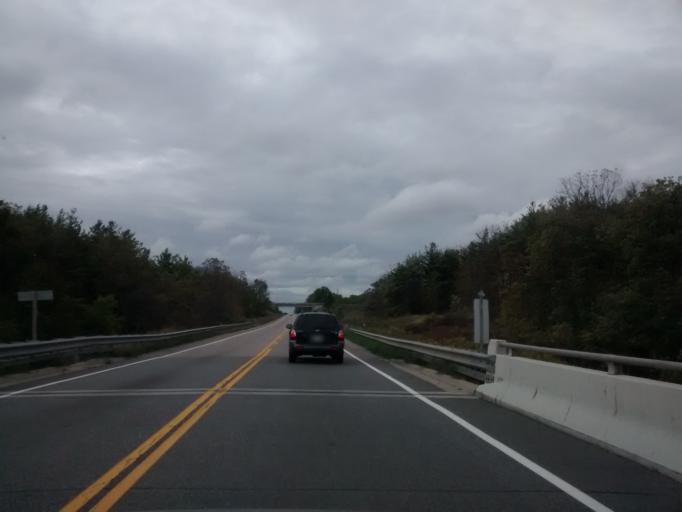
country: CA
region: Ontario
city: Ancaster
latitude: 43.0764
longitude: -79.9724
